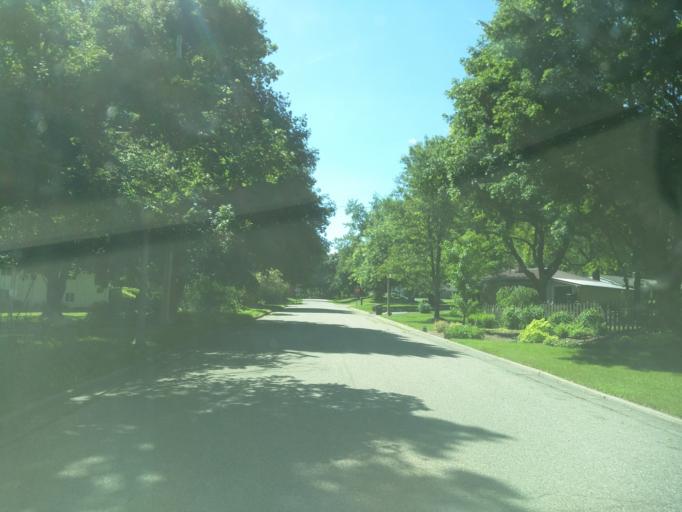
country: US
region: Michigan
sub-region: Ingham County
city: Edgemont Park
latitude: 42.7554
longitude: -84.5938
